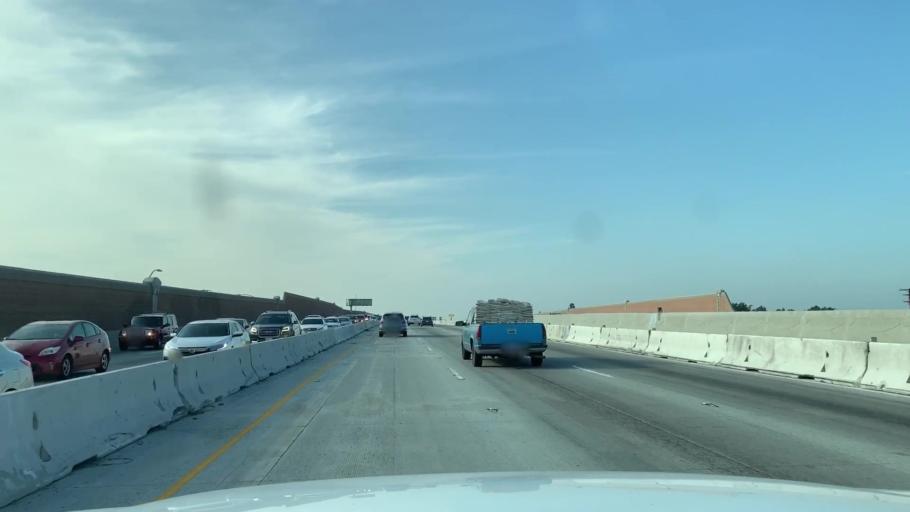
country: US
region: California
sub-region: Los Angeles County
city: Norwalk
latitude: 33.9118
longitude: -118.0731
